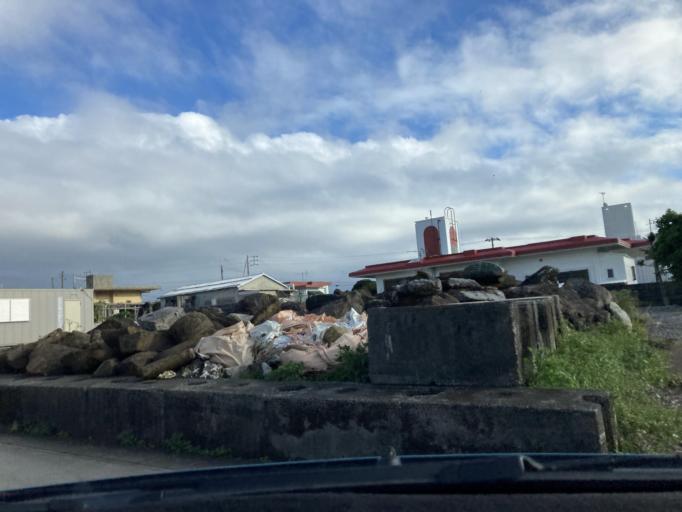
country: JP
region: Okinawa
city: Itoman
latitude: 26.1061
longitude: 127.6618
